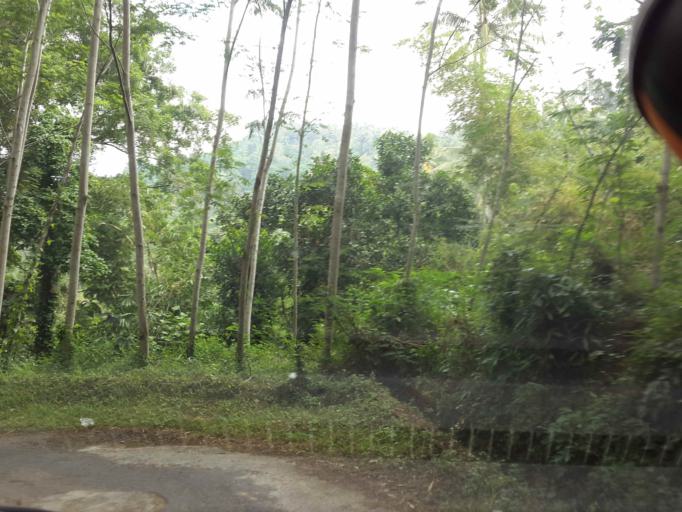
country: ID
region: Bali
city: Banjar Kelodan
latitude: -8.4864
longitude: 115.3863
